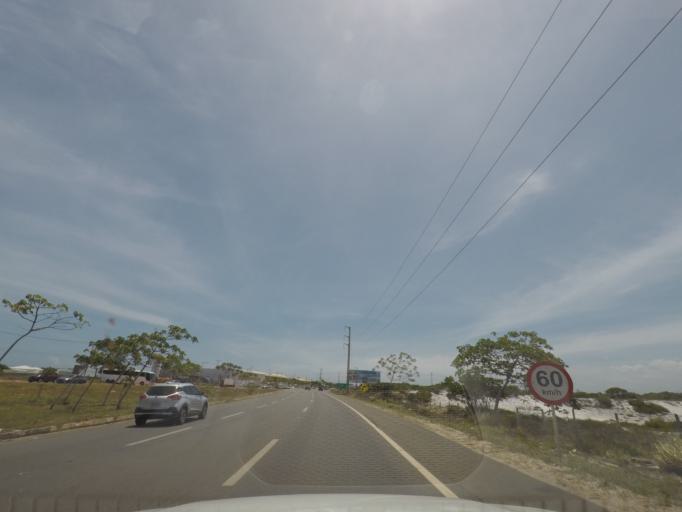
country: BR
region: Bahia
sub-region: Mata De Sao Joao
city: Mata de Sao Joao
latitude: -12.6403
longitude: -38.0728
